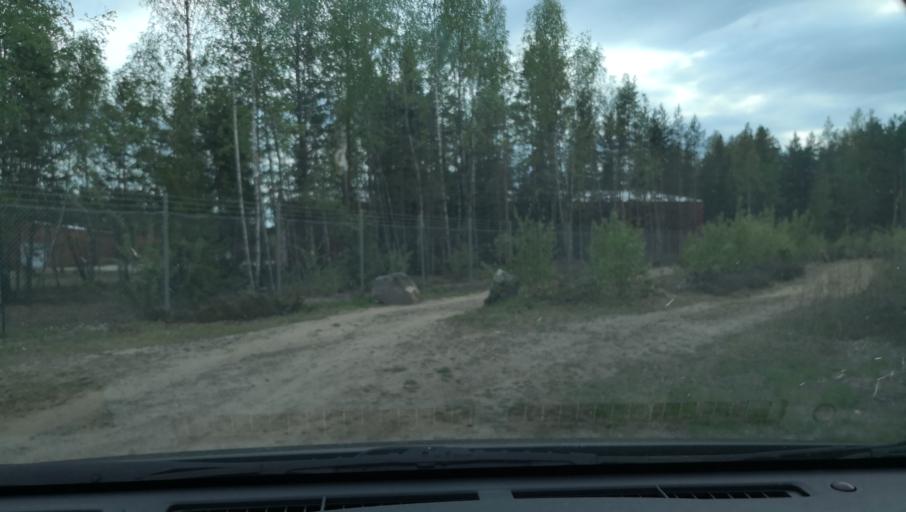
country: SE
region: Vaestmanland
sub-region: Skinnskattebergs Kommun
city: Skinnskatteberg
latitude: 59.8050
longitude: 15.5509
